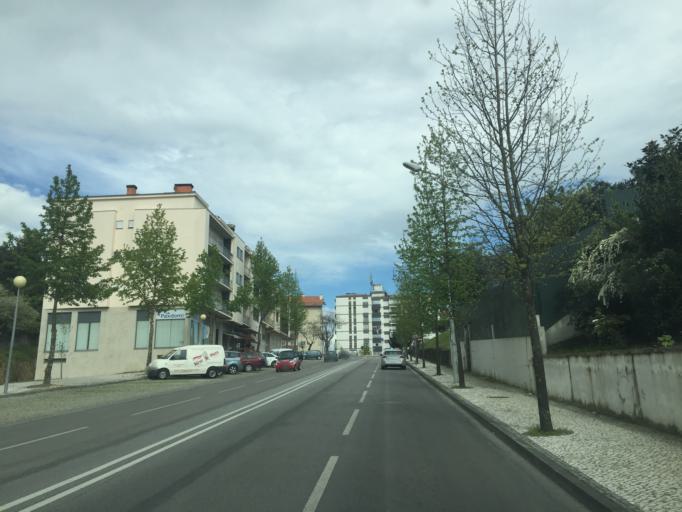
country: PT
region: Viseu
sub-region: Viseu
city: Viseu
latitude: 40.6598
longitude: -7.9253
